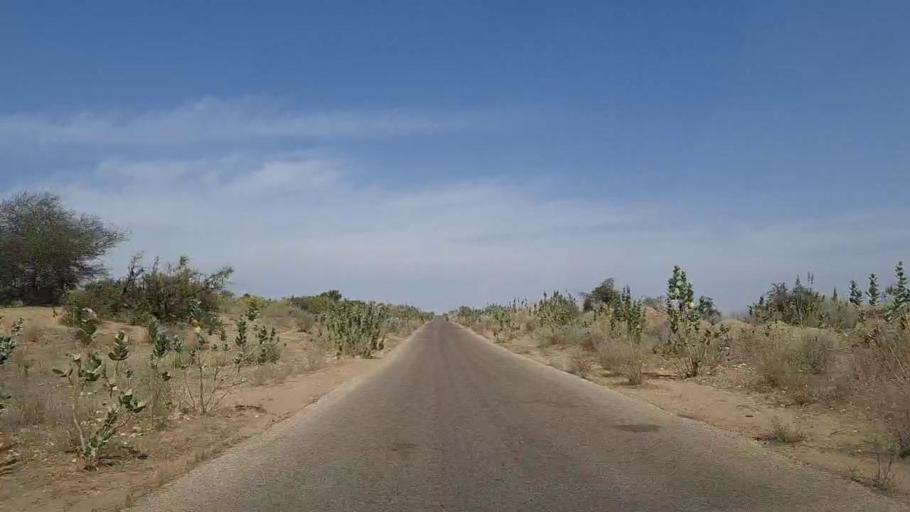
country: PK
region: Sindh
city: Umarkot
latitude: 25.1181
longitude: 69.9995
